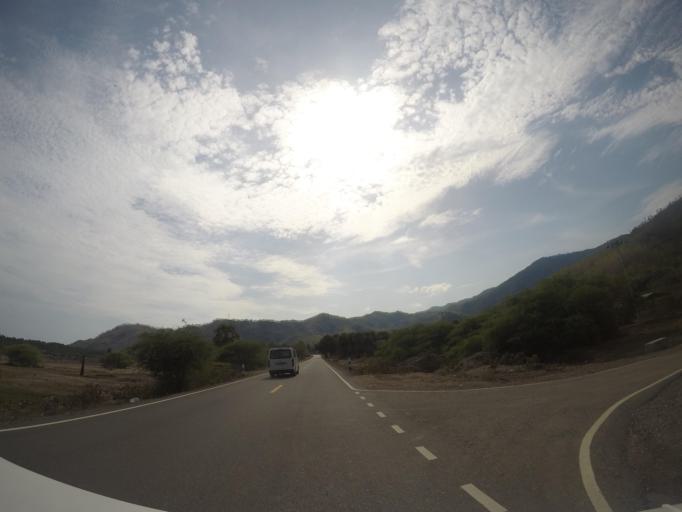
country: ID
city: Metinaro
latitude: -8.5374
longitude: 125.6985
